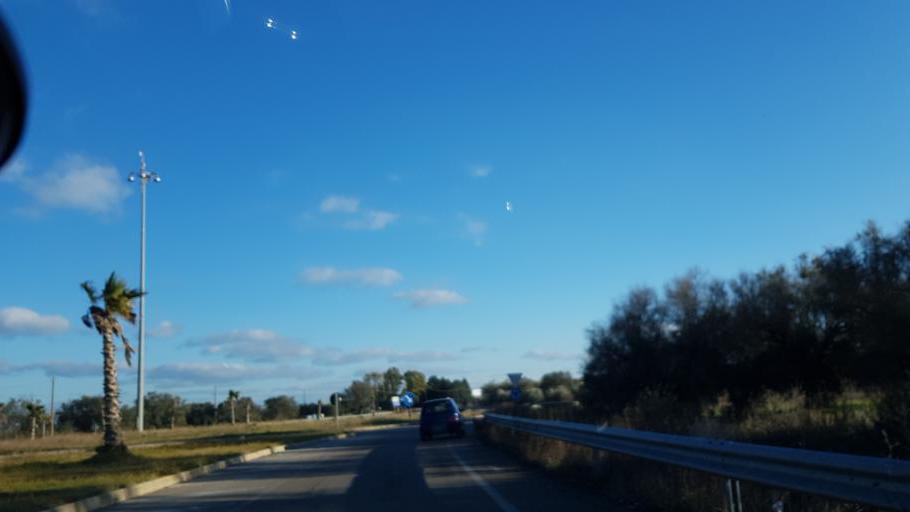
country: IT
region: Apulia
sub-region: Provincia di Brindisi
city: San Pietro Vernotico
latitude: 40.4769
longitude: 18.0070
